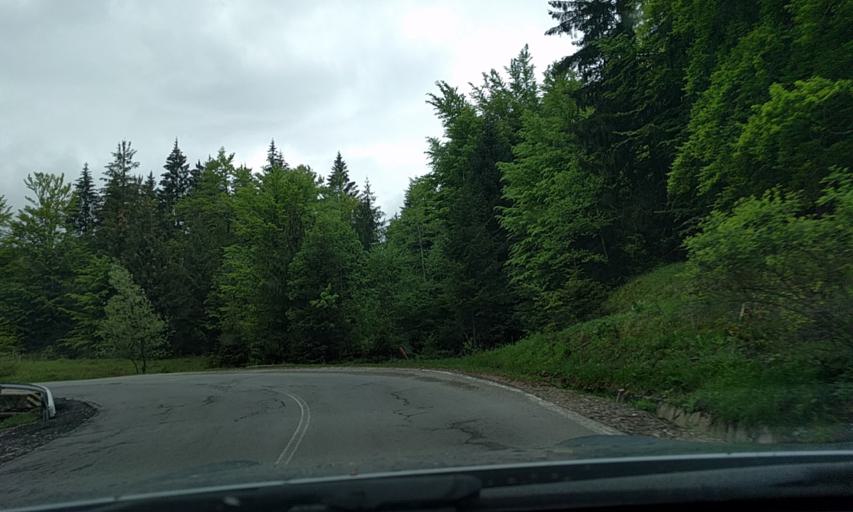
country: RO
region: Prahova
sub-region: Oras Sinaia
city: Sinaia
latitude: 45.3044
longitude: 25.5198
